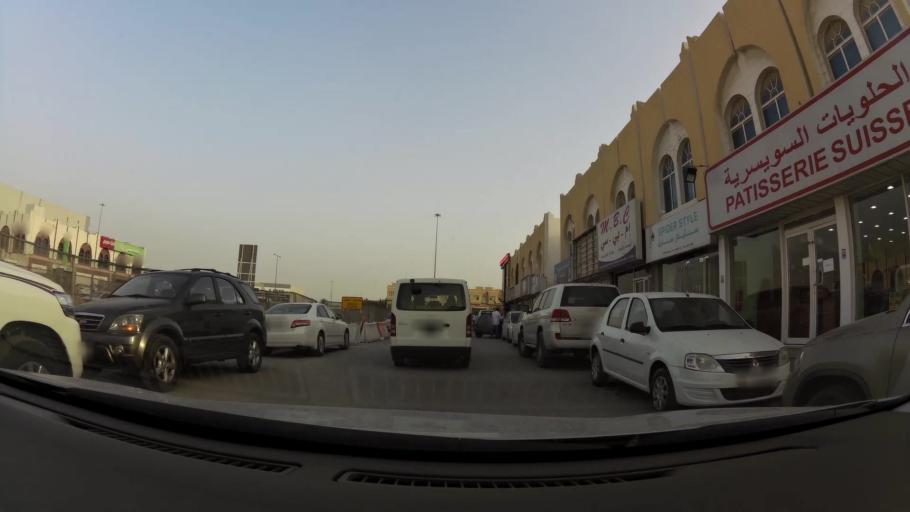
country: QA
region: Baladiyat ar Rayyan
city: Ar Rayyan
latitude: 25.2412
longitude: 51.4557
